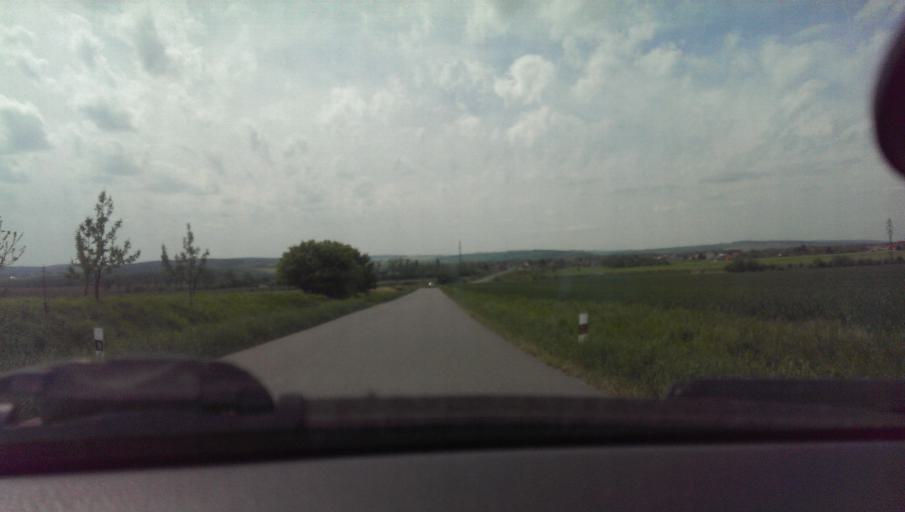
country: CZ
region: Zlin
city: Tlumacov
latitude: 49.2554
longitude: 17.5216
